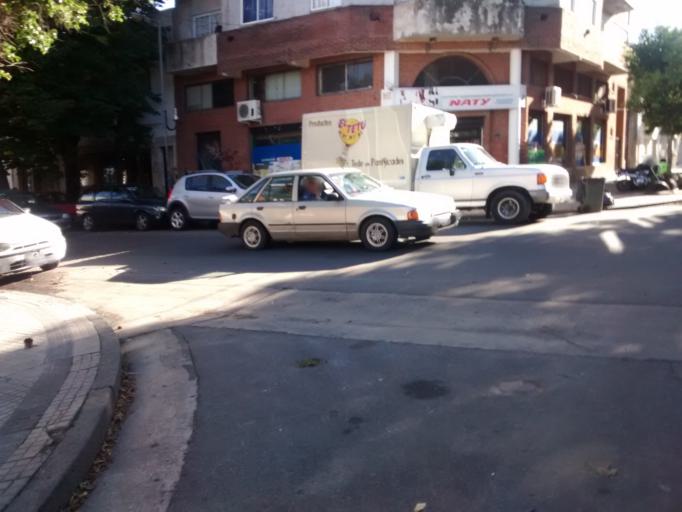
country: AR
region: Buenos Aires
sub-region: Partido de La Plata
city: La Plata
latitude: -34.9216
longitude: -57.9362
